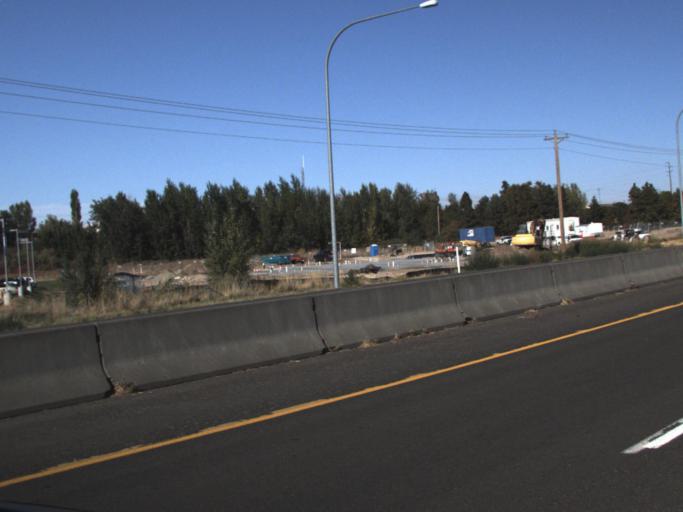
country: US
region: Washington
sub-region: Walla Walla County
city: College Place
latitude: 46.0383
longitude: -118.3685
